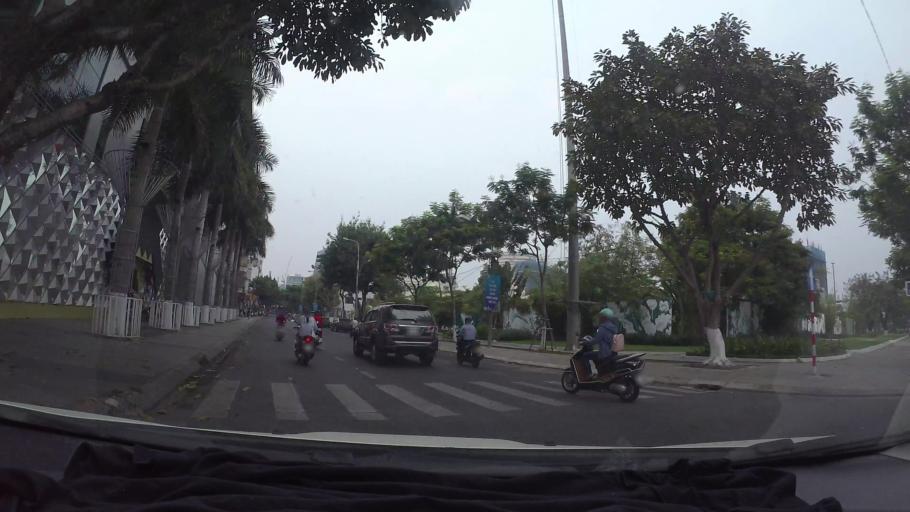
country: VN
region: Da Nang
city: Da Nang
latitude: 16.0687
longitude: 108.2210
